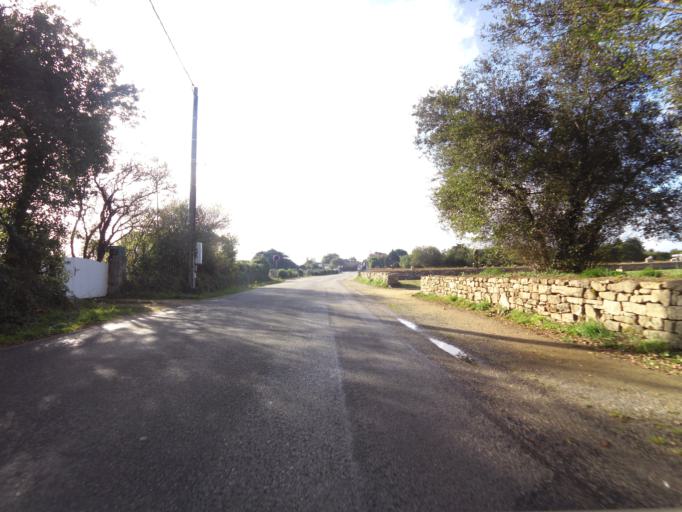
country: FR
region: Brittany
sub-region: Departement du Morbihan
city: Carnac
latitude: 47.5939
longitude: -3.0811
